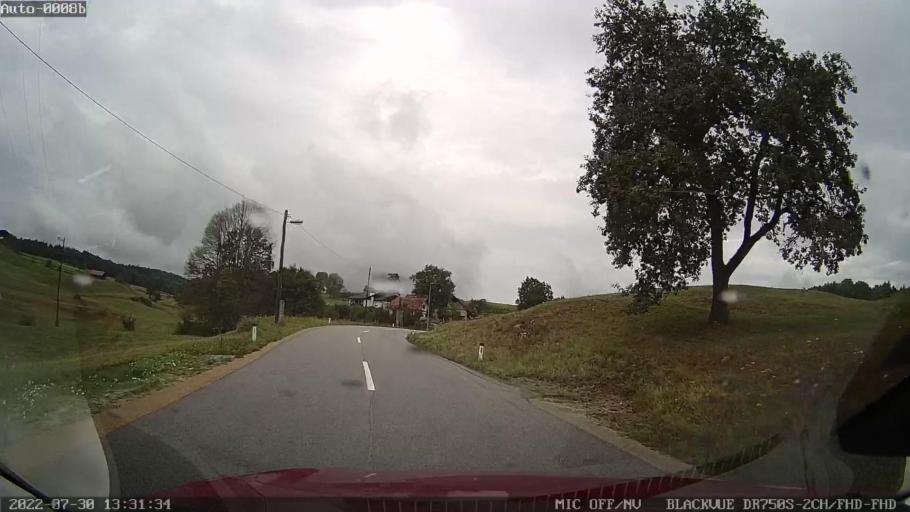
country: SI
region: Zuzemberk
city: Zuzemberk
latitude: 45.8375
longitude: 14.9362
